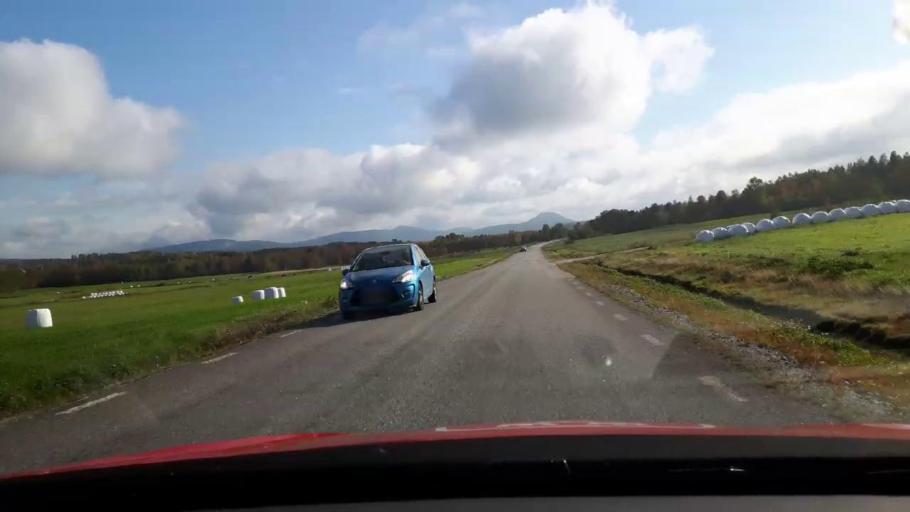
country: SE
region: Gaevleborg
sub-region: Ljusdals Kommun
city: Ljusdal
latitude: 61.7610
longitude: 16.0855
